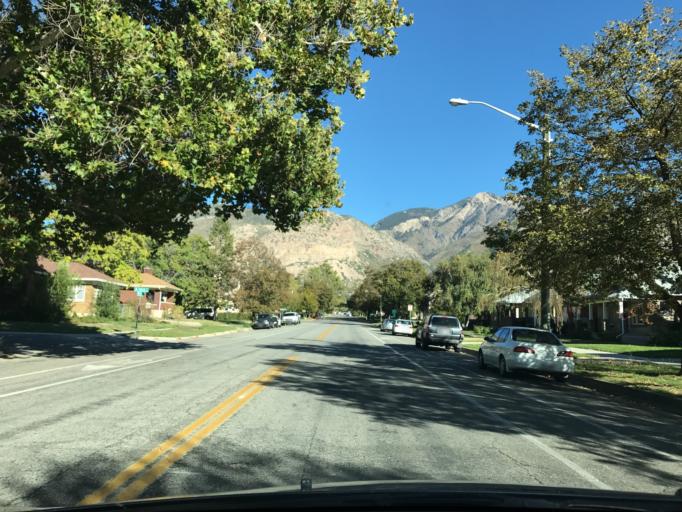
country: US
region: Utah
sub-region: Weber County
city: Ogden
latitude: 41.2184
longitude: -111.9556
